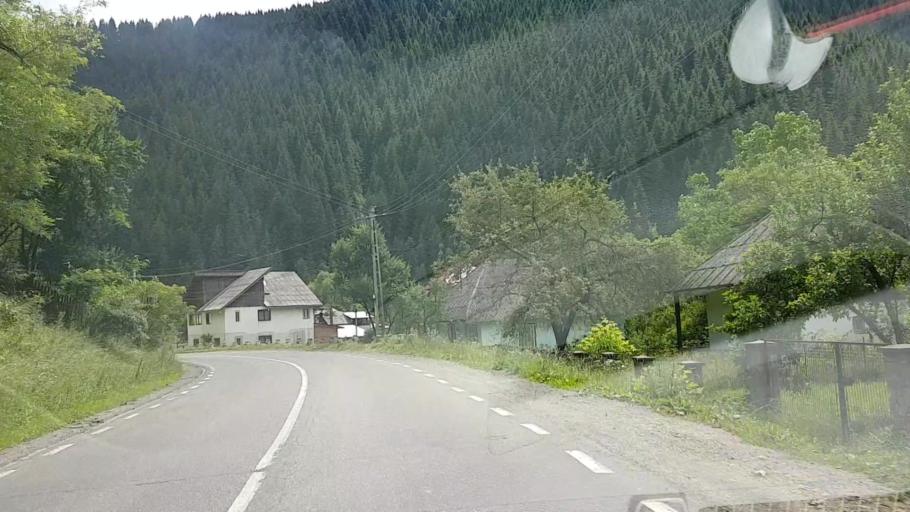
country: RO
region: Suceava
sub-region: Comuna Brosteni
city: Brosteni
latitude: 47.2175
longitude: 25.7380
